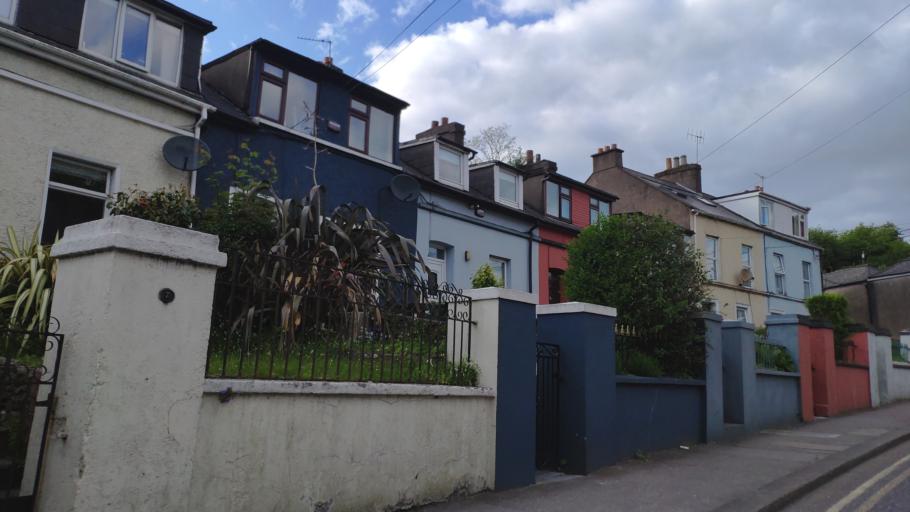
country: IE
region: Munster
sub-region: County Cork
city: Cork
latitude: 51.9067
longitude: -8.4577
